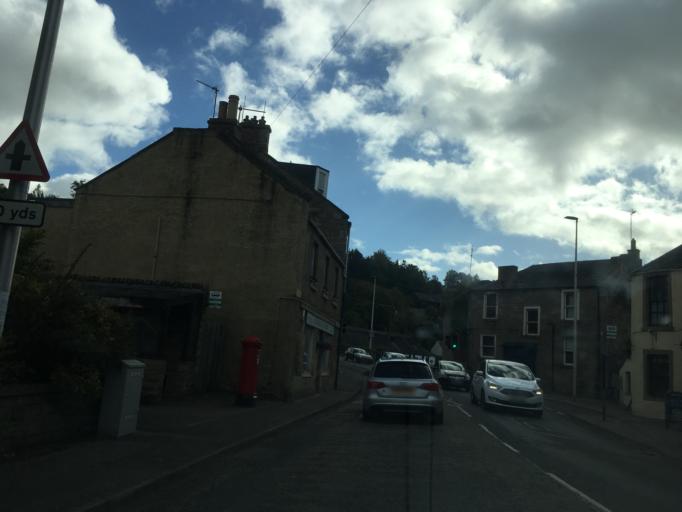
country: GB
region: Scotland
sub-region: Midlothian
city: Bonnyrigg
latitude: 55.8837
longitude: -3.1153
